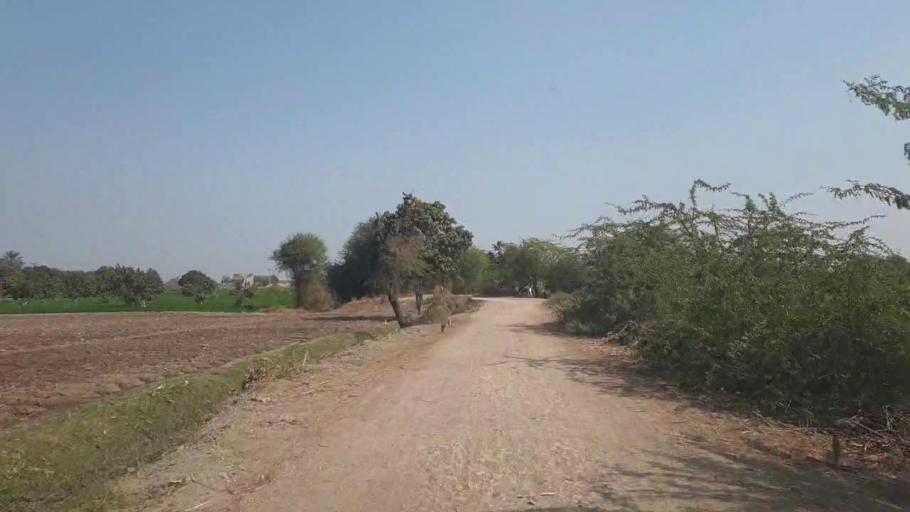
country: PK
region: Sindh
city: Mirpur Khas
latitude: 25.4886
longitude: 68.8824
